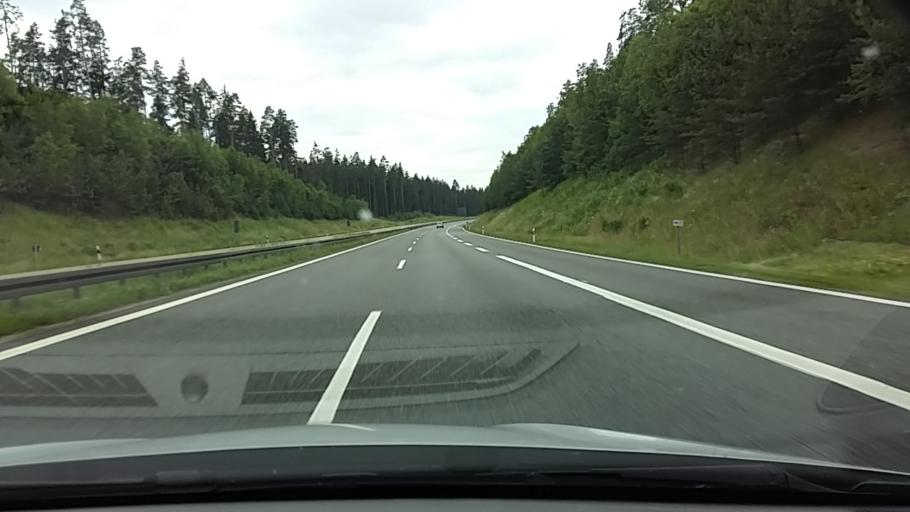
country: DE
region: Bavaria
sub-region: Upper Palatinate
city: Moosbach
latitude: 49.6173
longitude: 12.4138
